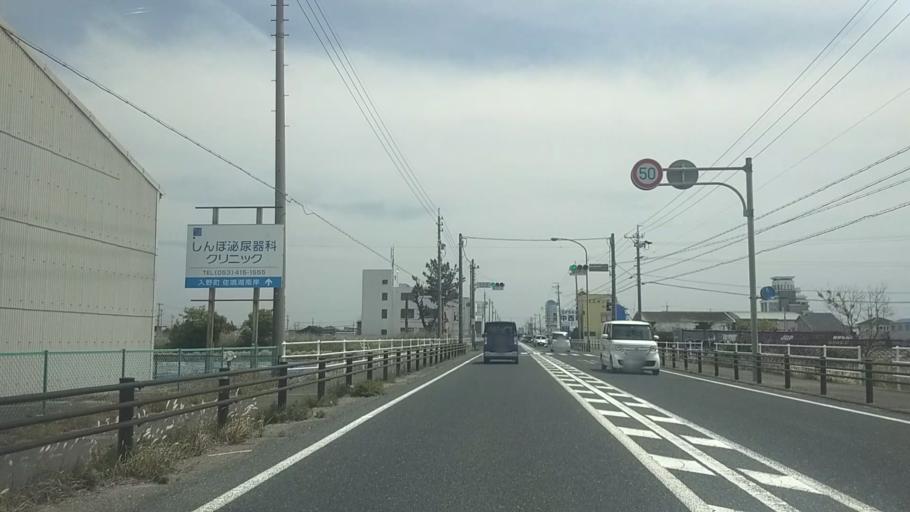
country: JP
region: Shizuoka
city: Hamamatsu
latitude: 34.6807
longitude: 137.6416
